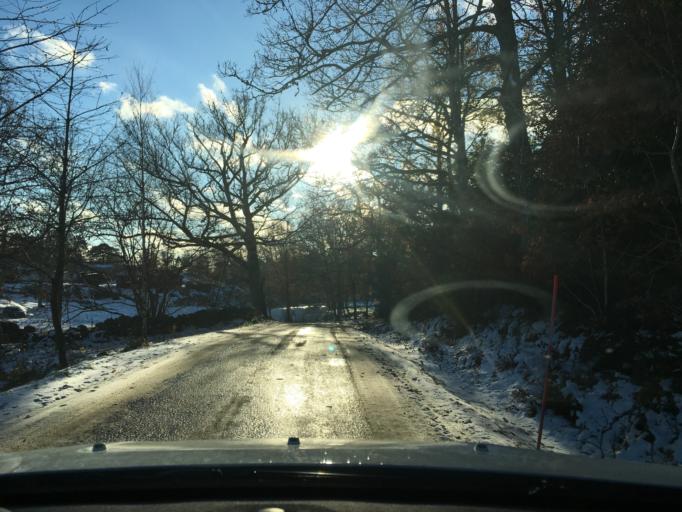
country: SE
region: Vaestra Goetaland
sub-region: Tjorns Kommun
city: Myggenas
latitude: 58.0905
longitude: 11.7537
